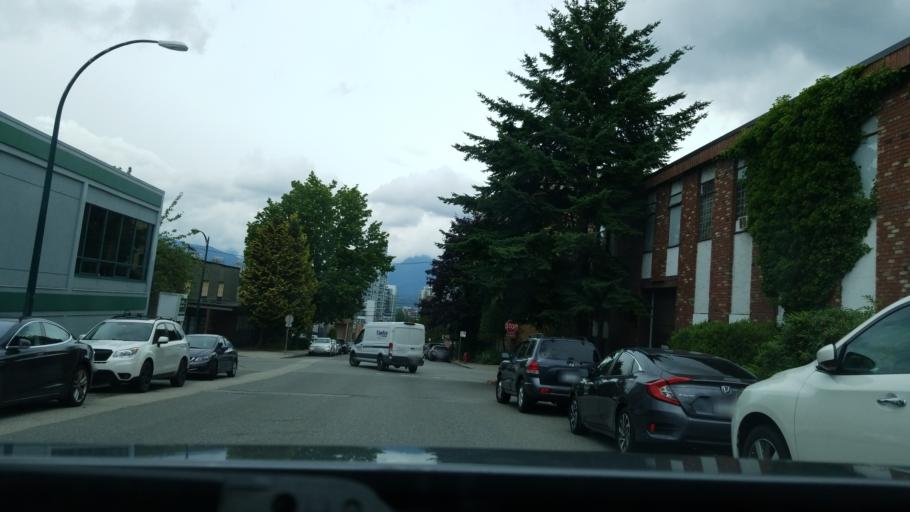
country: CA
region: British Columbia
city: Vancouver
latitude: 49.2642
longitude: -123.1029
